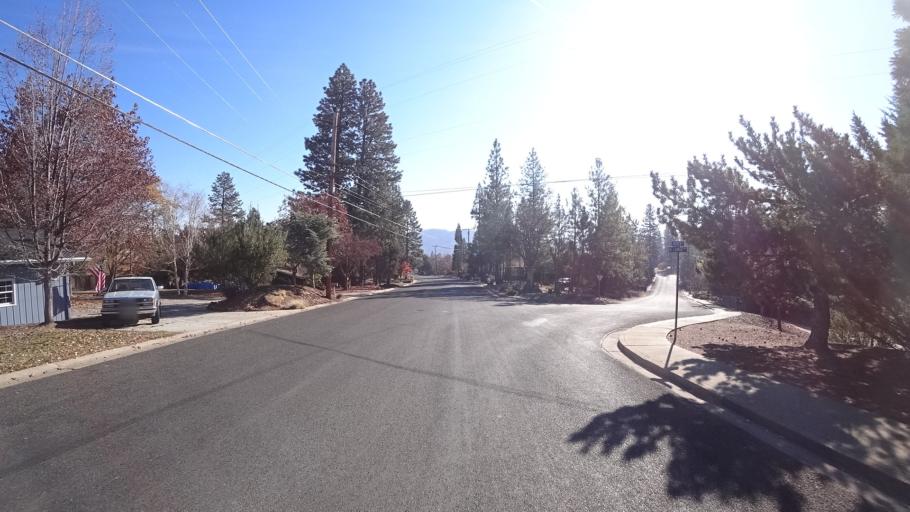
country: US
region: California
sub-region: Siskiyou County
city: Yreka
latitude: 41.7372
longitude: -122.6548
